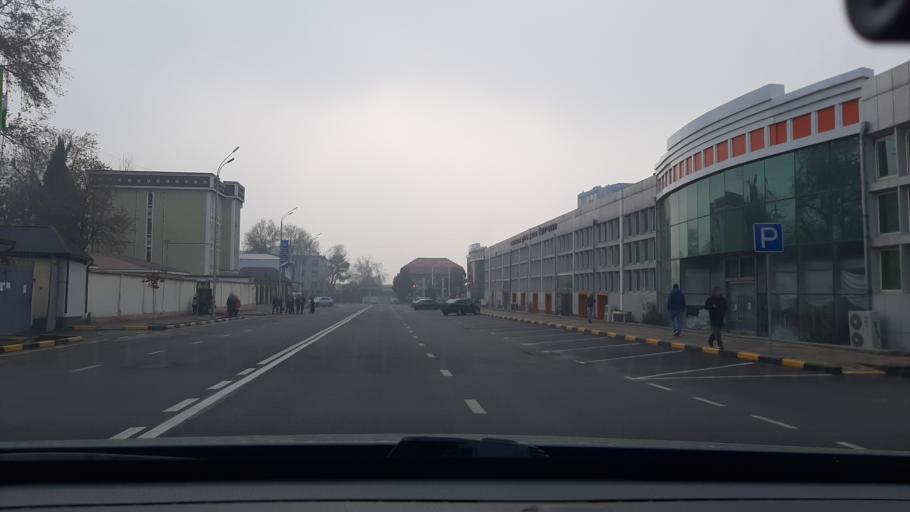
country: TJ
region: Dushanbe
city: Dushanbe
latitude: 38.5591
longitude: 68.7955
